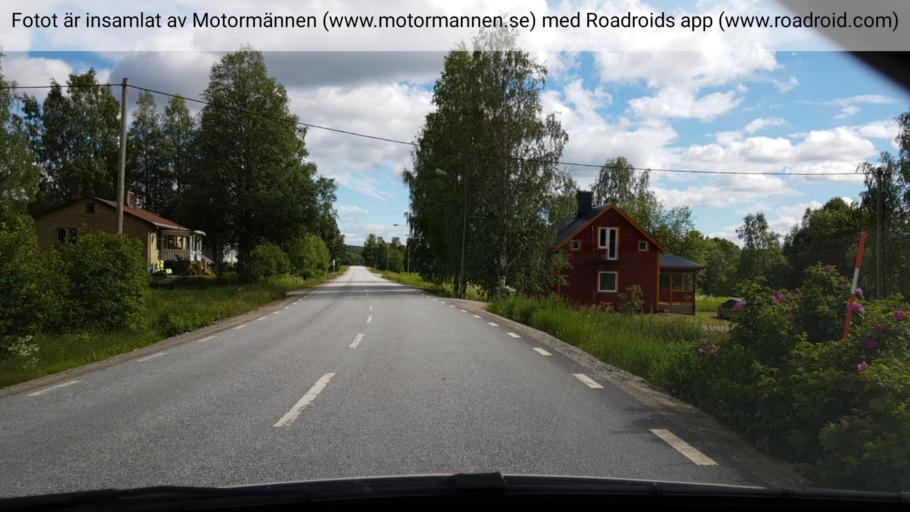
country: SE
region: Vaesterbotten
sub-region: Vindelns Kommun
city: Vindeln
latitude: 64.1624
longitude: 19.4996
